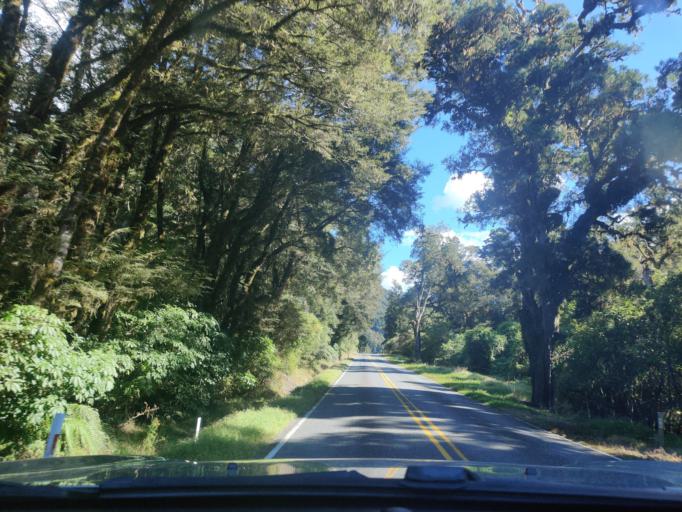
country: NZ
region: Otago
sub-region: Queenstown-Lakes District
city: Wanaka
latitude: -43.9692
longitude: 169.3797
